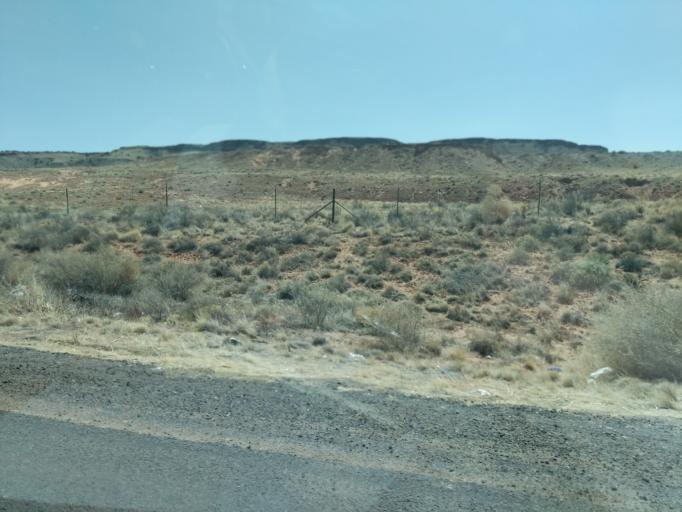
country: US
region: Arizona
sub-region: Navajo County
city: Dilkon
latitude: 35.4487
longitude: -110.0653
